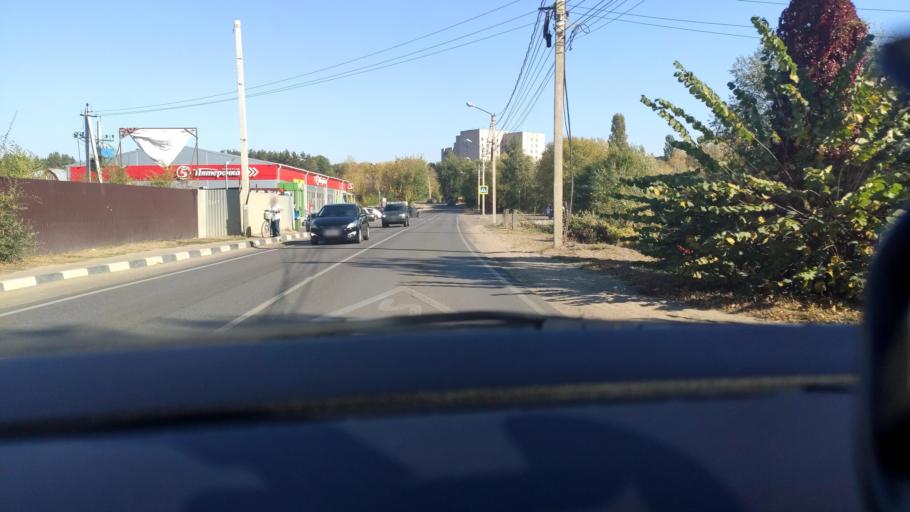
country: RU
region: Voronezj
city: Pridonskoy
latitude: 51.6442
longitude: 39.0958
